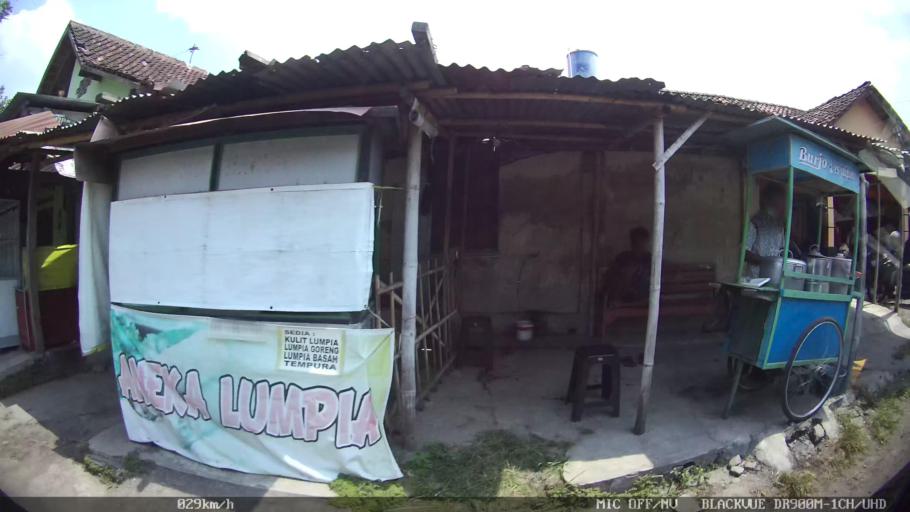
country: ID
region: Daerah Istimewa Yogyakarta
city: Yogyakarta
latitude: -7.8223
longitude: 110.4075
